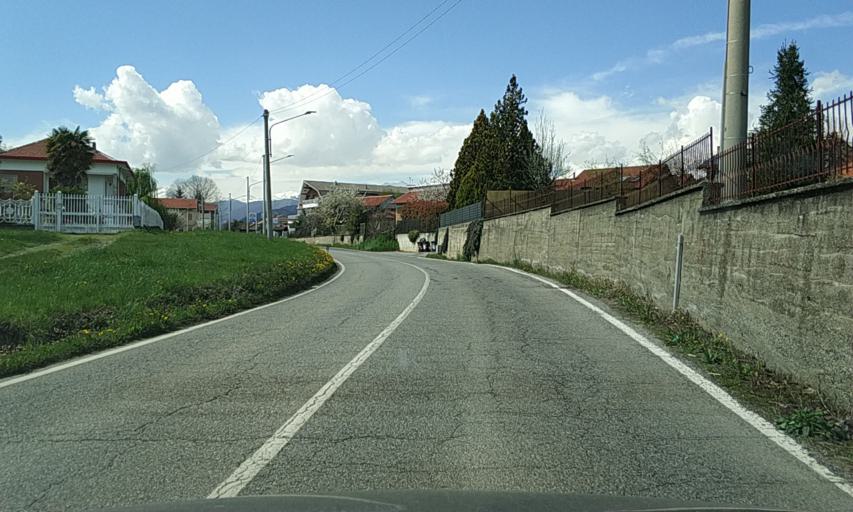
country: IT
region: Piedmont
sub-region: Provincia di Torino
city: San Carlo Canavese
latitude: 45.2500
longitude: 7.5952
